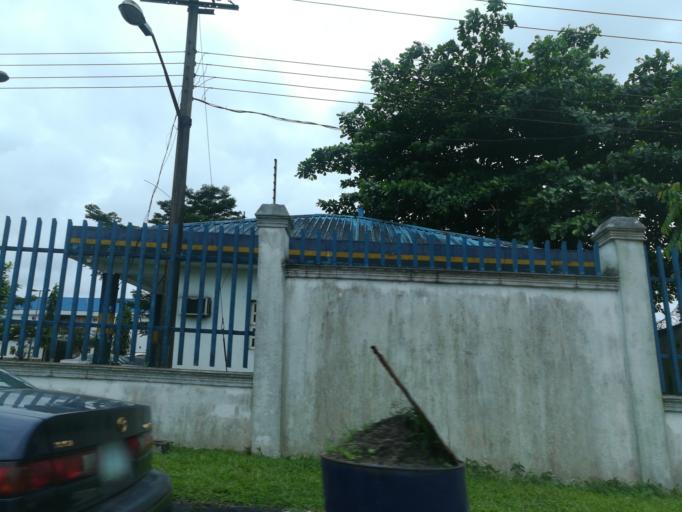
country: NG
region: Rivers
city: Port Harcourt
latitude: 4.7685
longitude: 7.0206
